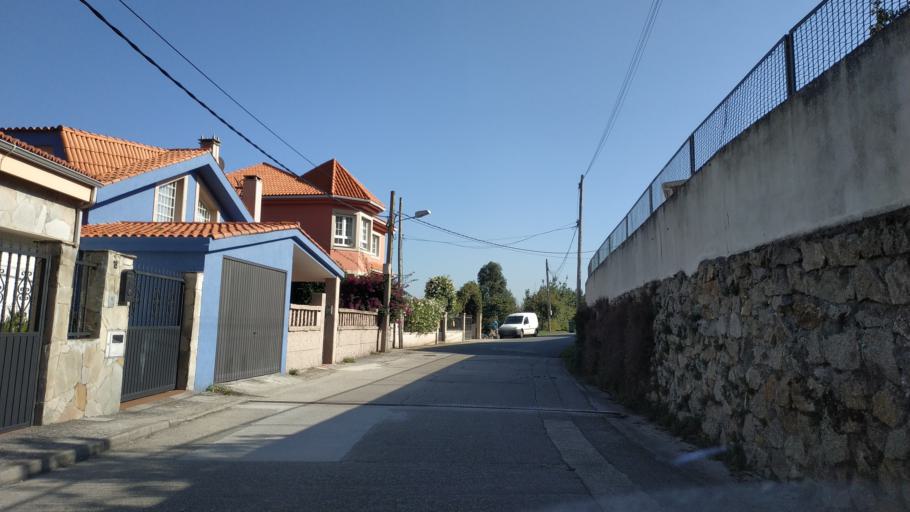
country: ES
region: Galicia
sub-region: Provincia da Coruna
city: Culleredo
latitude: 43.3255
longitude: -8.3880
